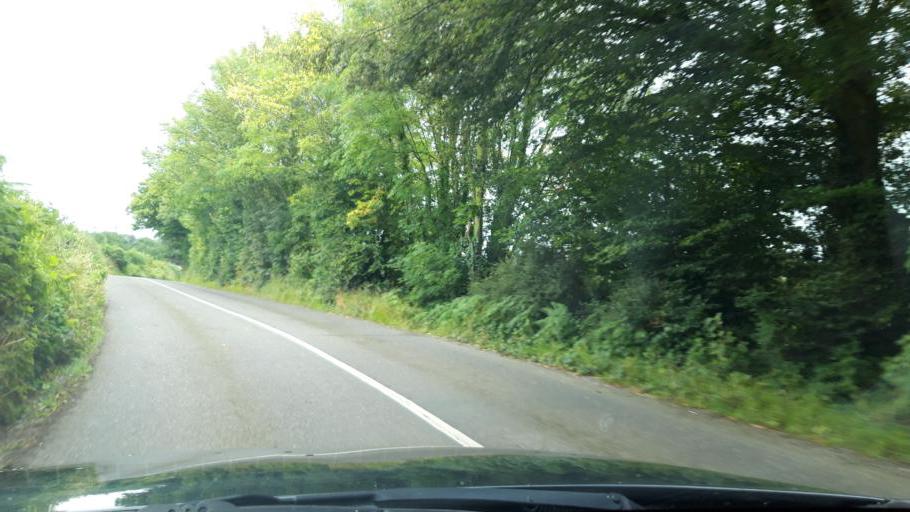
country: IE
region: Munster
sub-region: County Cork
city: Youghal
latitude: 52.1308
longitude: -7.9909
